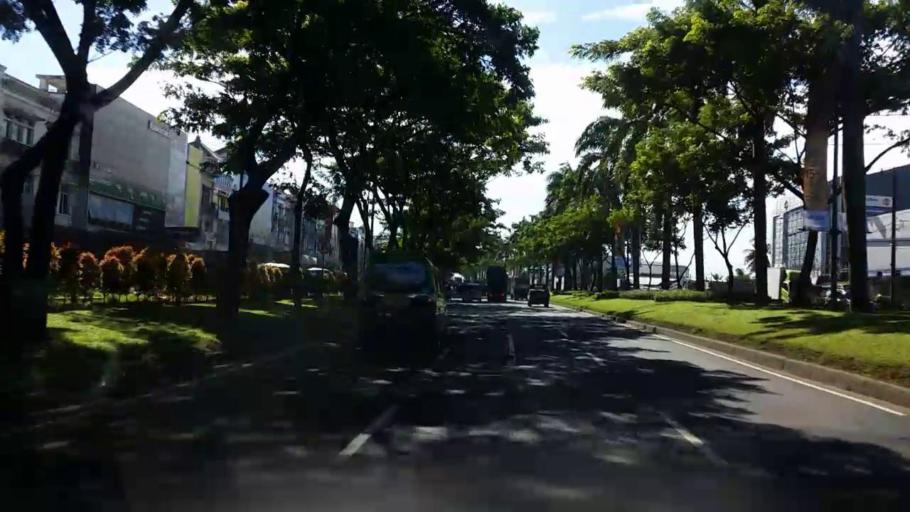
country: ID
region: West Java
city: Serpong
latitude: -6.3048
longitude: 106.6694
